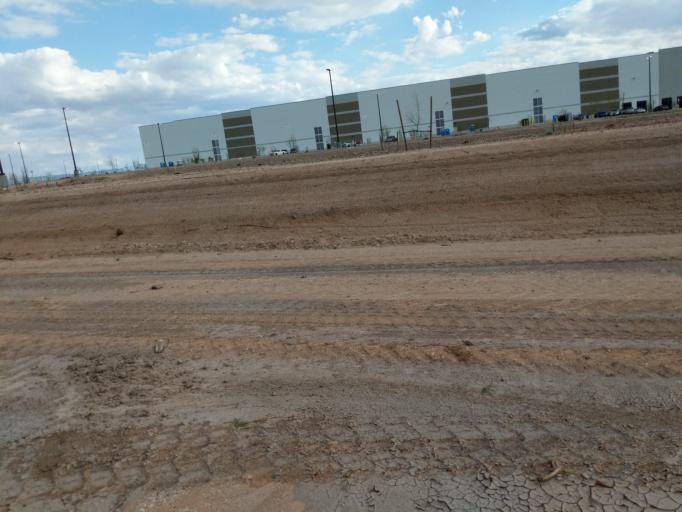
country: US
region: Arizona
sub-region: Pima County
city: Tucson
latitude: 32.1335
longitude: -110.8388
